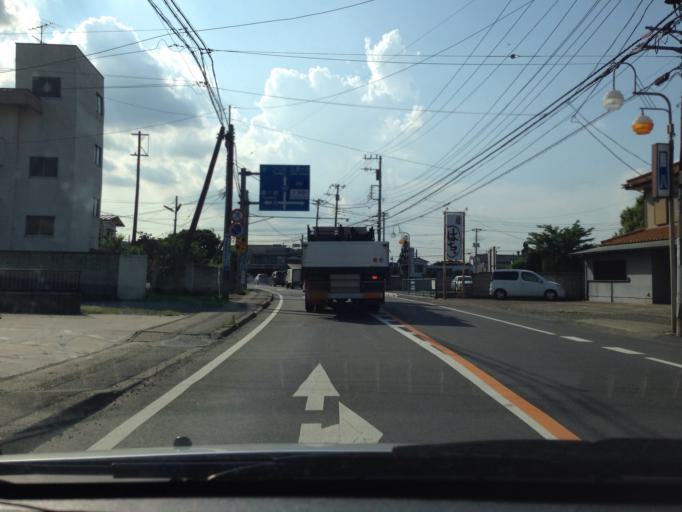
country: JP
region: Ibaraki
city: Ami
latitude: 36.0696
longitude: 140.2027
